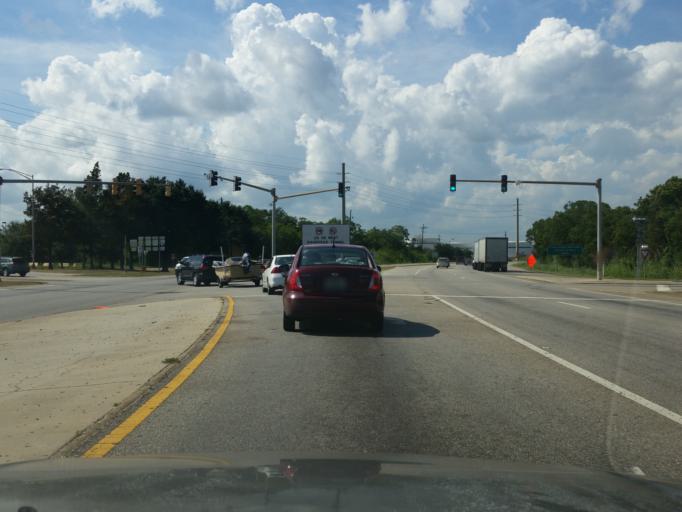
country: US
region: Alabama
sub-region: Mobile County
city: Mobile
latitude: 30.6930
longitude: -88.0296
